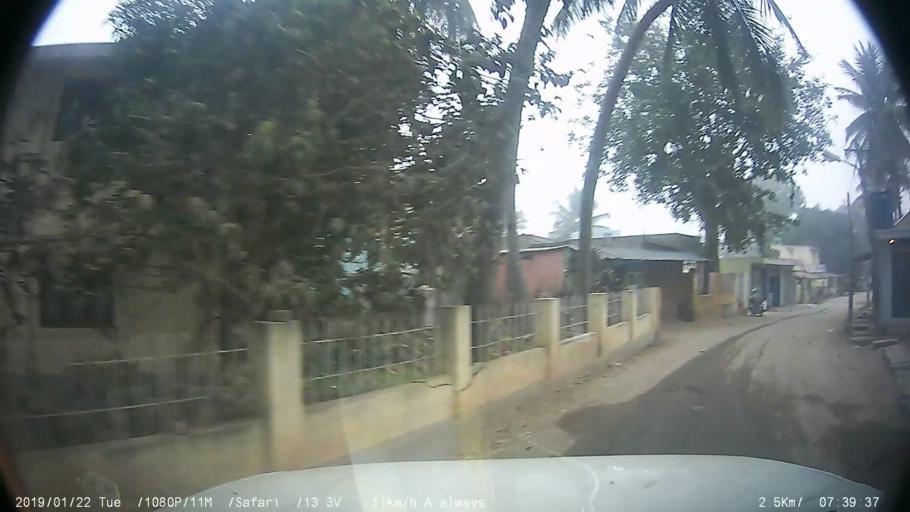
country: IN
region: Karnataka
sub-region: Bangalore Urban
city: Anekal
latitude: 12.8178
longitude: 77.6371
